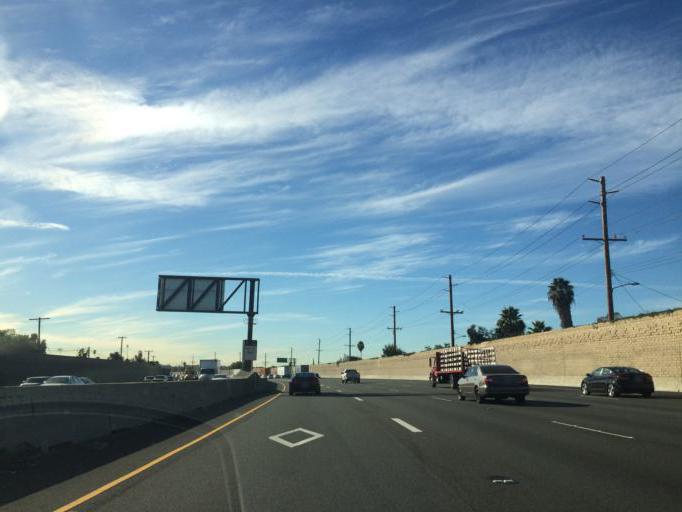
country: US
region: California
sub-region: Los Angeles County
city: Claremont
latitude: 34.0817
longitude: -117.7311
